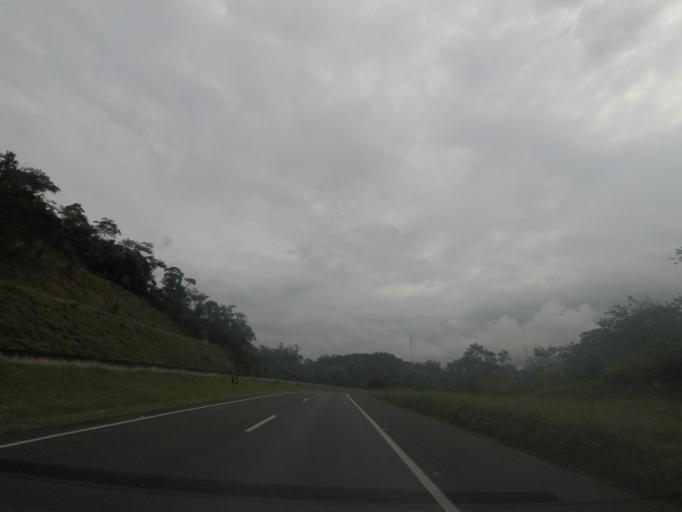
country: BR
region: Sao Paulo
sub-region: Cajati
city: Cajati
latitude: -24.7482
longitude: -48.1501
